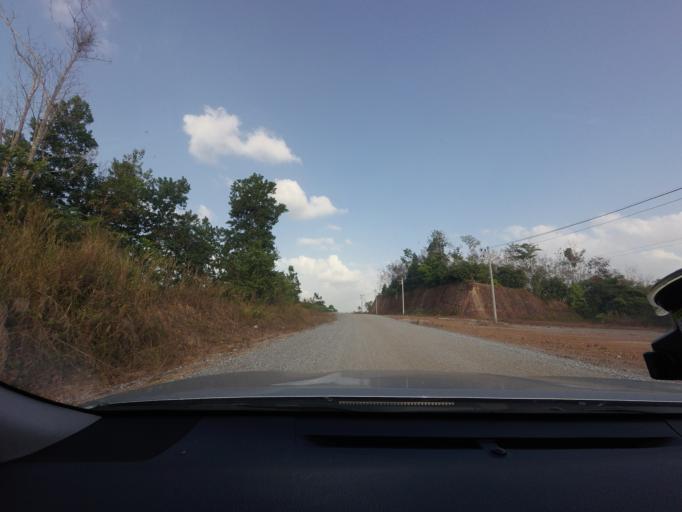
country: TH
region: Pattani
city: Mae Lan
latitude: 6.6056
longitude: 101.2448
